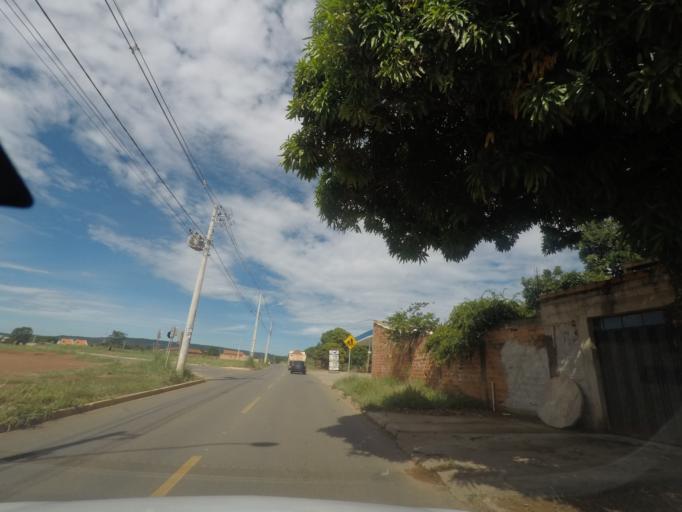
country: BR
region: Goias
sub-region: Aparecida De Goiania
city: Aparecida de Goiania
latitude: -16.8131
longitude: -49.2860
